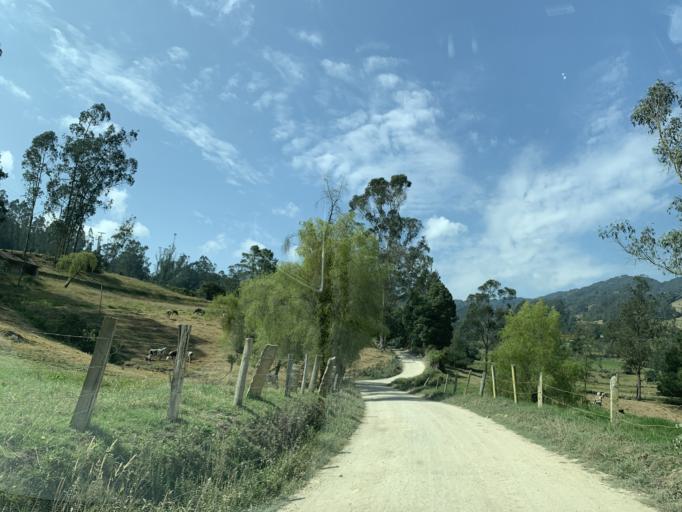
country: CO
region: Boyaca
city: Turmeque
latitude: 5.2813
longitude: -73.5046
